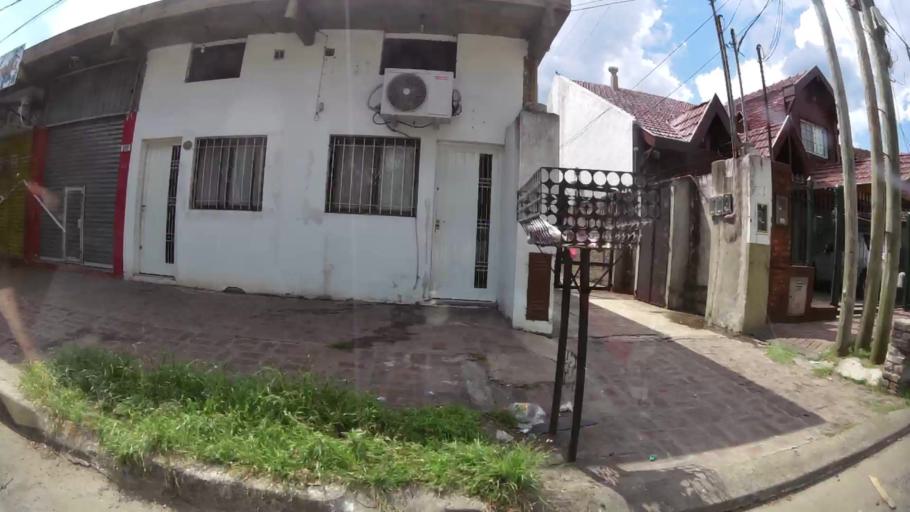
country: AR
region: Buenos Aires
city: Ituzaingo
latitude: -34.6407
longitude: -58.6703
